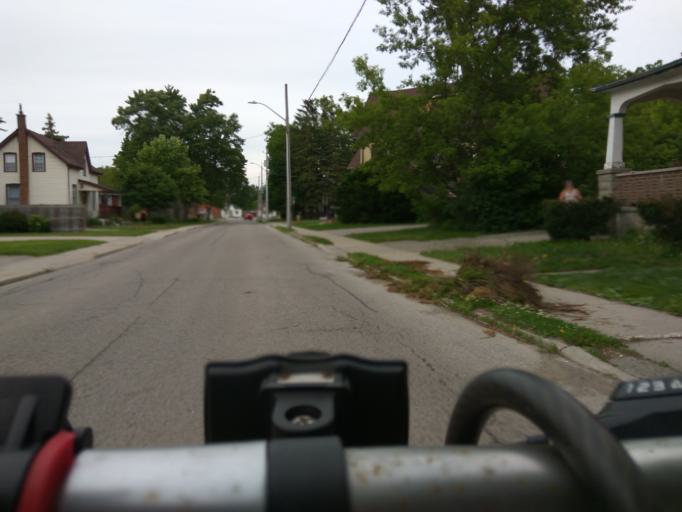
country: CA
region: Ontario
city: Stratford
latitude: 43.3618
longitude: -80.9848
